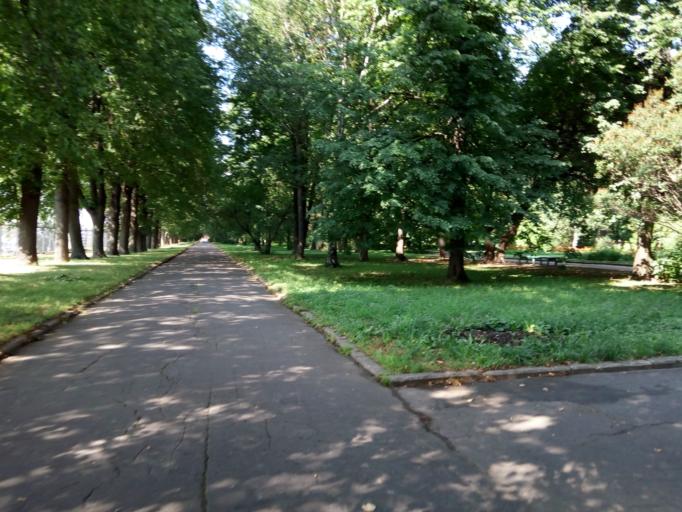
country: RU
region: Moskovskaya
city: Levoberezhnyy
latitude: 55.8528
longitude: 37.4661
